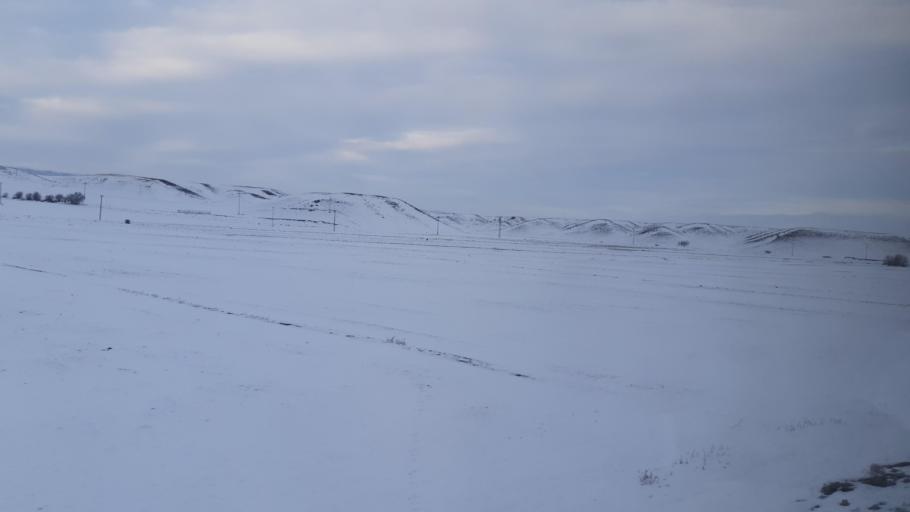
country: TR
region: Kirsehir
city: Mecidiye
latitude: 39.6880
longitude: 34.3905
